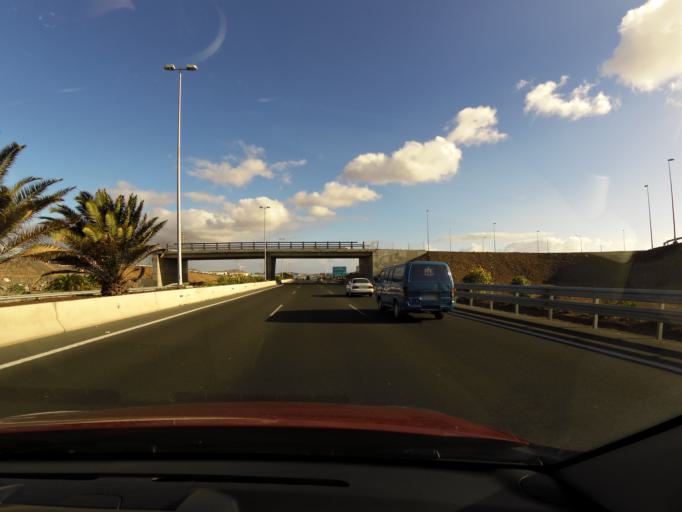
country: ES
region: Canary Islands
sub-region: Provincia de Las Palmas
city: Cruce de Arinaga
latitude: 27.8523
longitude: -15.4309
